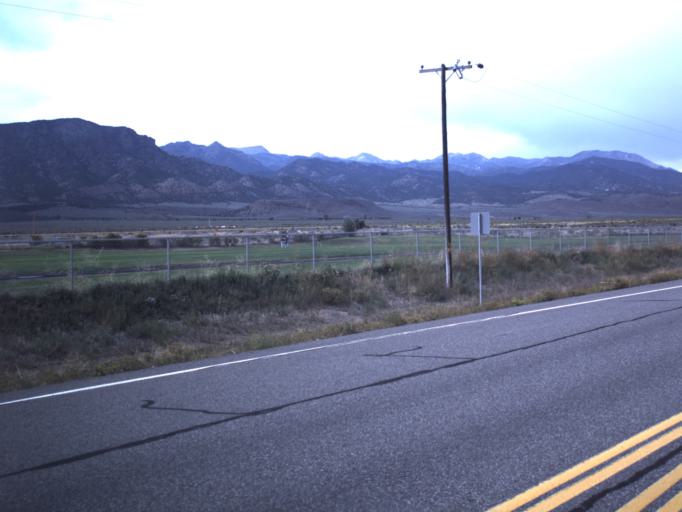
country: US
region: Utah
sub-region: Piute County
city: Junction
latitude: 38.2463
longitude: -112.2201
